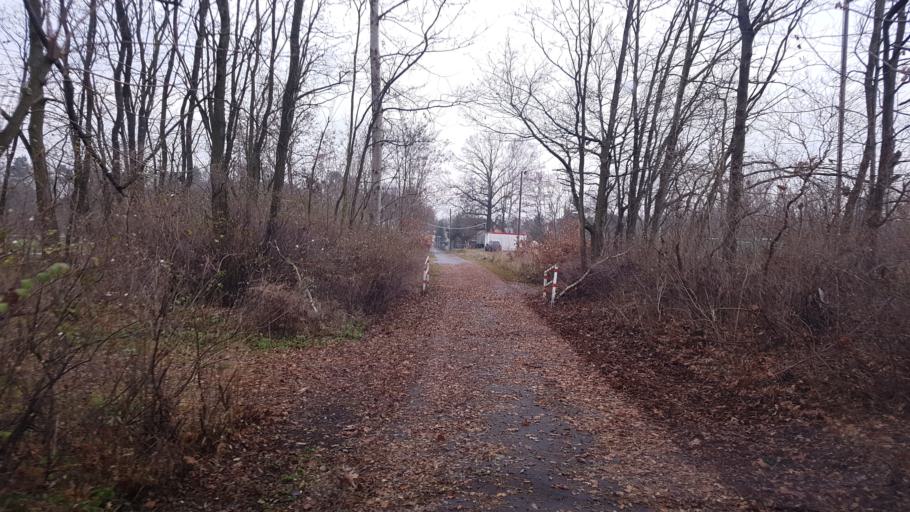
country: DE
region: Brandenburg
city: Sallgast
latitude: 51.5632
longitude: 13.8724
